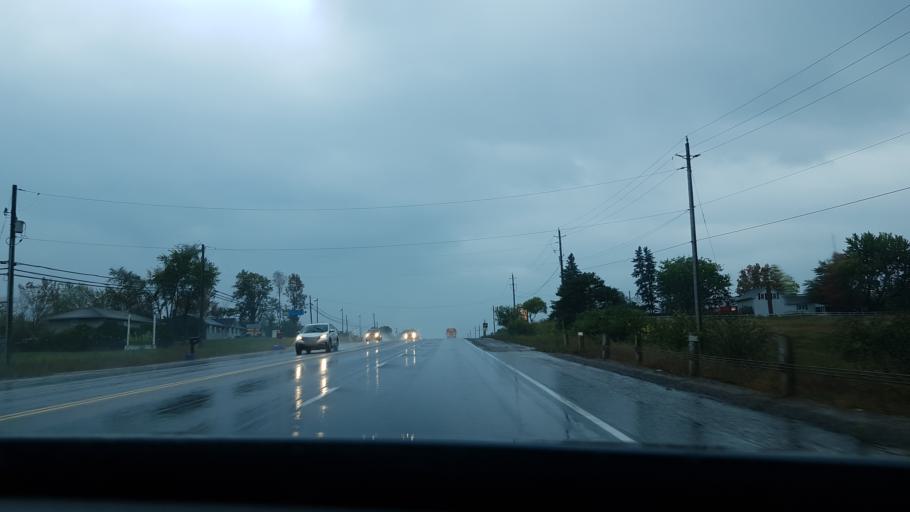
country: CA
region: Ontario
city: Peterborough
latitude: 44.3455
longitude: -78.3582
